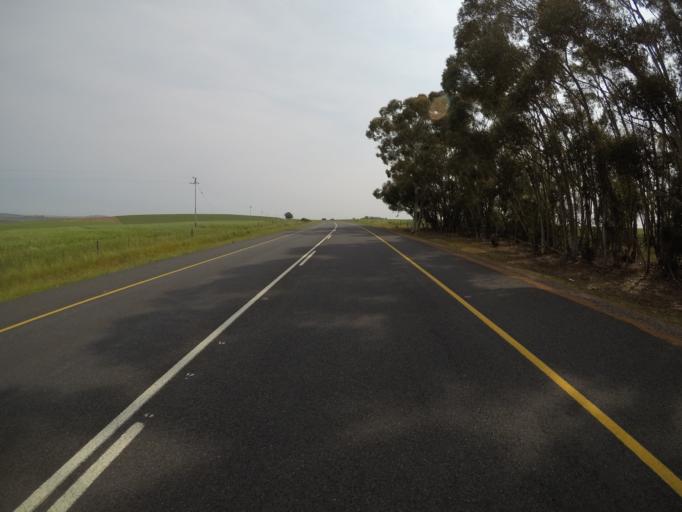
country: ZA
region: Western Cape
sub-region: West Coast District Municipality
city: Malmesbury
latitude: -33.5112
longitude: 18.8446
